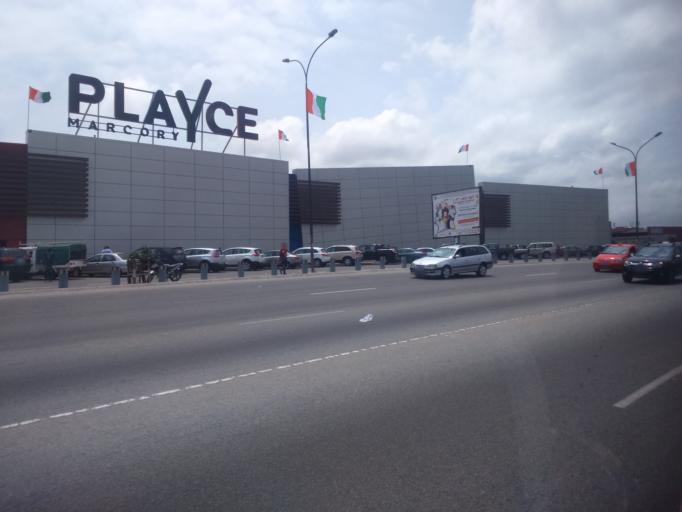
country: CI
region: Lagunes
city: Abidjan
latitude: 5.3016
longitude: -3.9923
